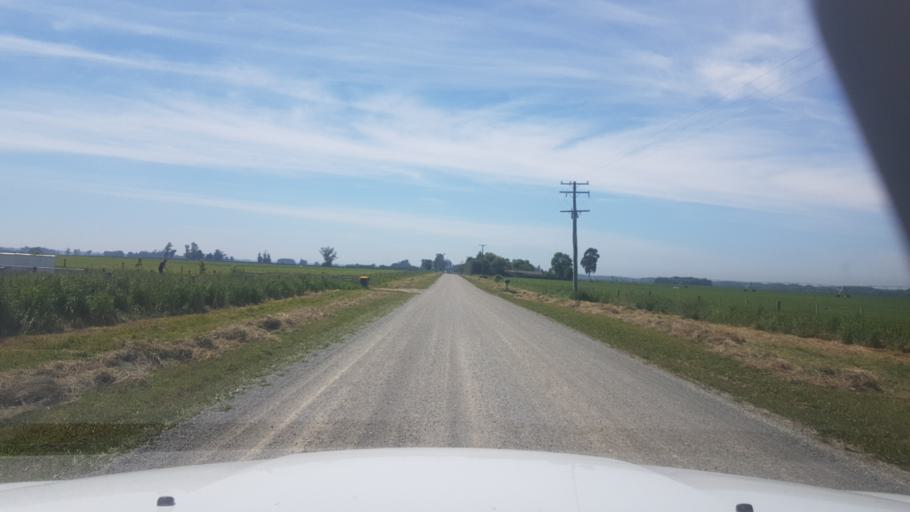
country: NZ
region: Canterbury
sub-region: Timaru District
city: Pleasant Point
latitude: -44.2420
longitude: 171.1592
